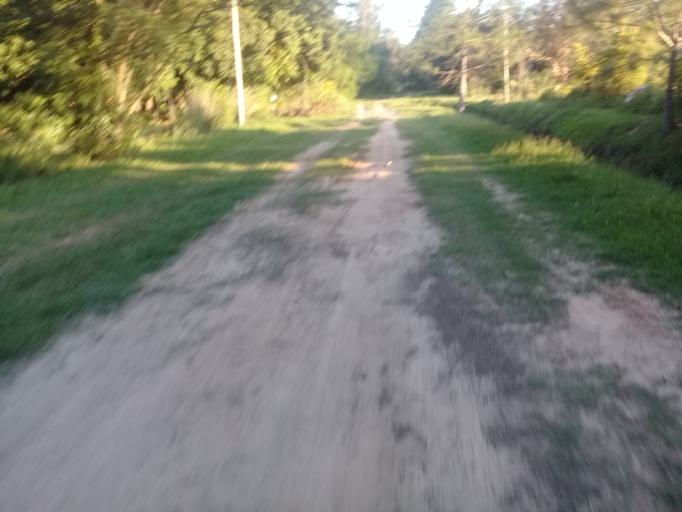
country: AR
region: Corrientes
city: San Luis del Palmar
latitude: -27.4673
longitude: -58.6661
